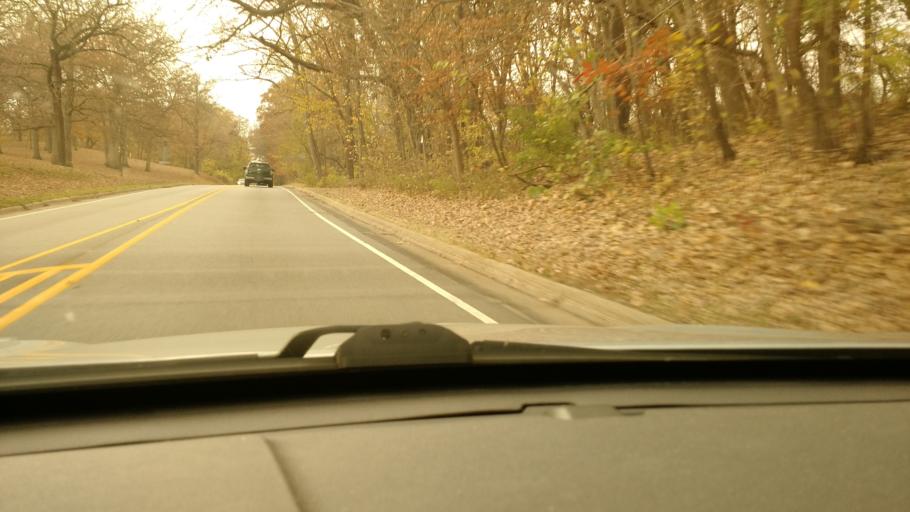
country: US
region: Illinois
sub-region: Rock Island County
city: Milan
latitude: 41.4649
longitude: -90.5674
